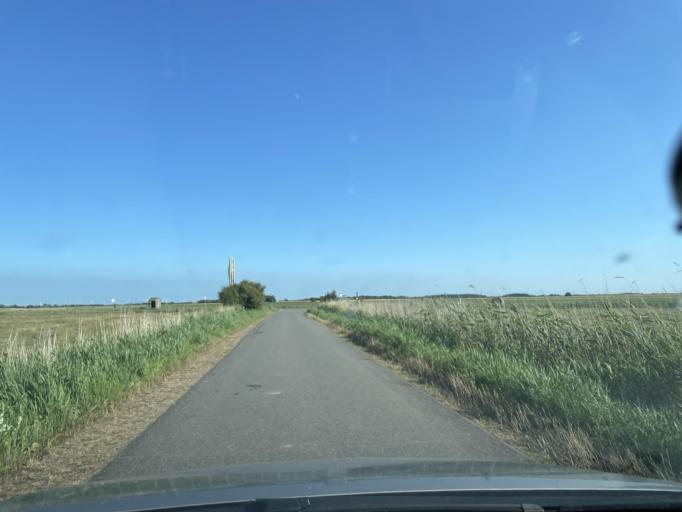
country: DE
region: Schleswig-Holstein
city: Neukirchen
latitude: 54.8792
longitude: 8.7747
